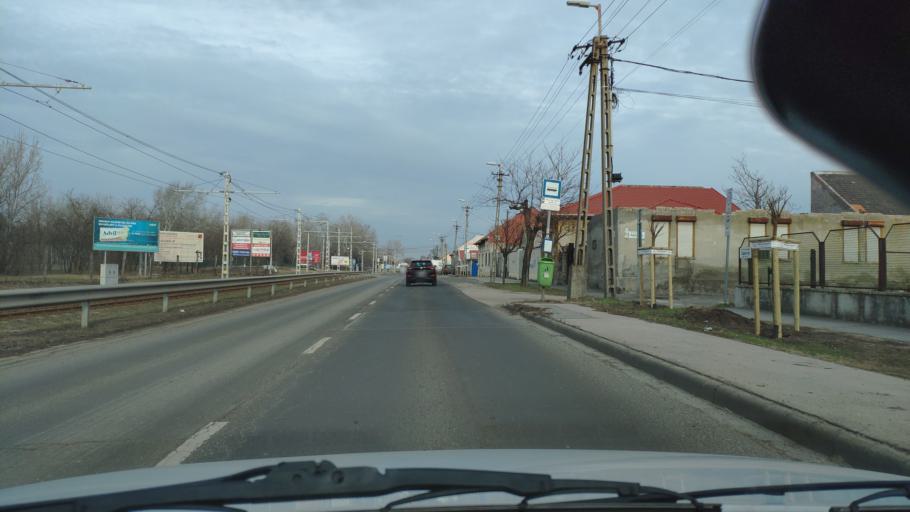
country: HU
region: Budapest
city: Budapest XX. keruelet
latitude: 47.4477
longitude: 19.1028
